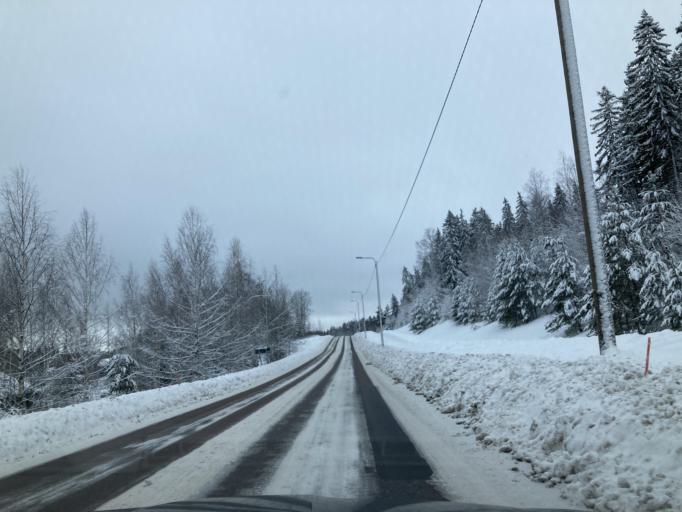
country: FI
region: Central Finland
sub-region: Jaemsae
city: Jaemsae
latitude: 61.8795
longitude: 25.2830
